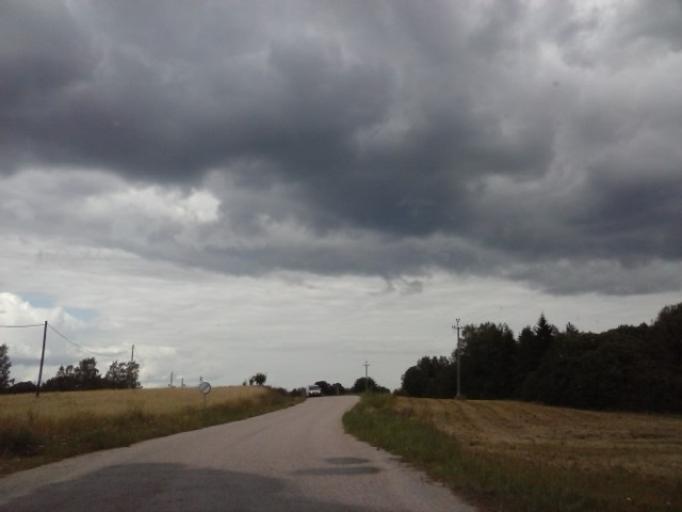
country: EE
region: Vorumaa
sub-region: Voru linn
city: Voru
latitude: 57.7420
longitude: 27.1108
